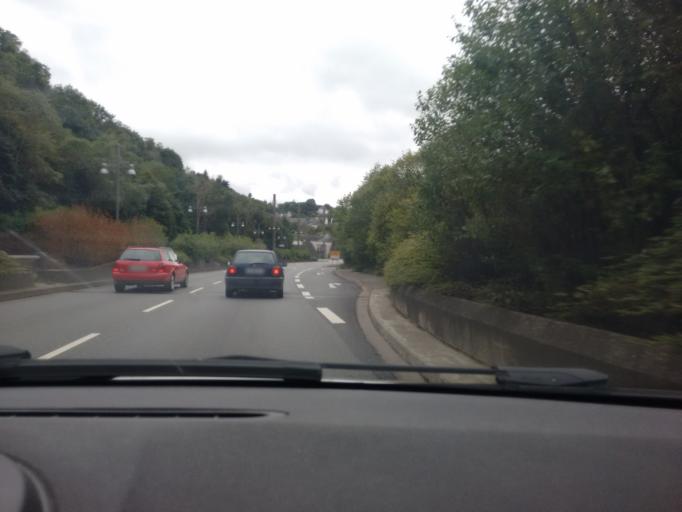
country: DE
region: Rheinland-Pfalz
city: Hintertiefenbach
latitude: 49.7027
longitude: 7.3394
